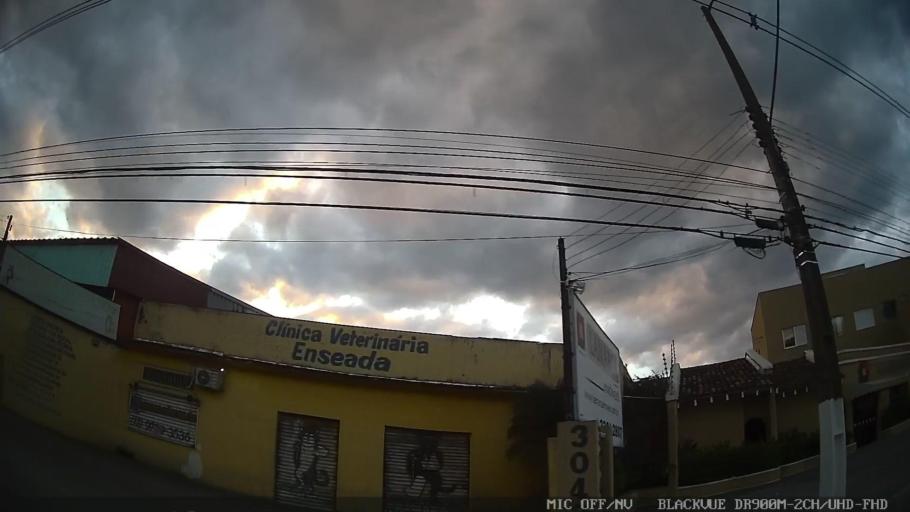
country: BR
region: Sao Paulo
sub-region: Guaruja
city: Guaruja
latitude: -23.9787
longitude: -46.2247
